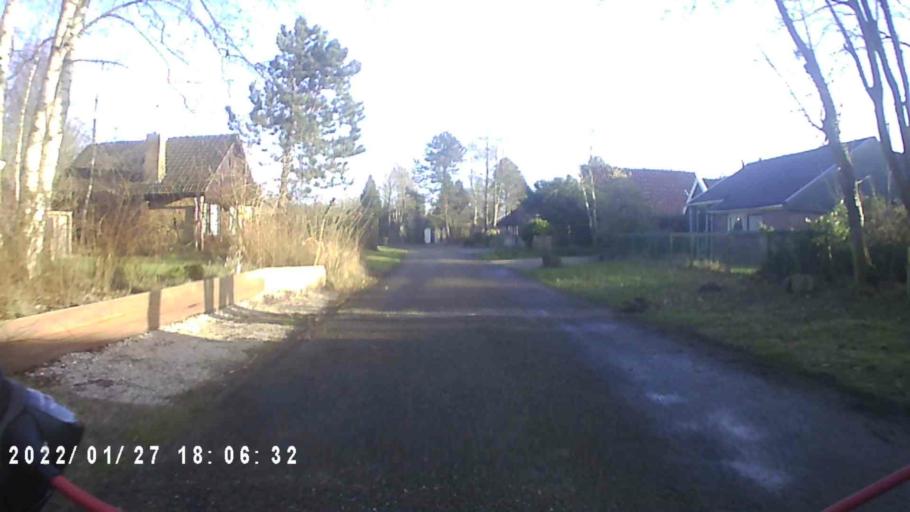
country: NL
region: Friesland
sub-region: Gemeente Dongeradeel
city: Anjum
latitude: 53.4057
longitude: 6.2185
